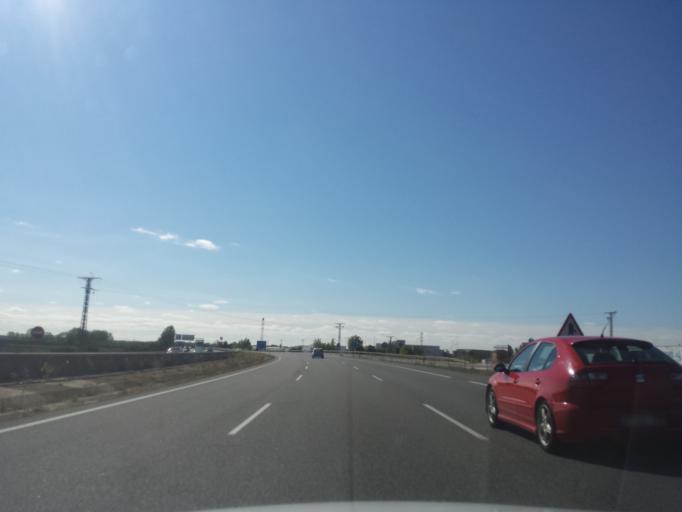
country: ES
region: Castille and Leon
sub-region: Provincia de Zamora
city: Benavente
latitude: 41.9987
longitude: -5.6553
